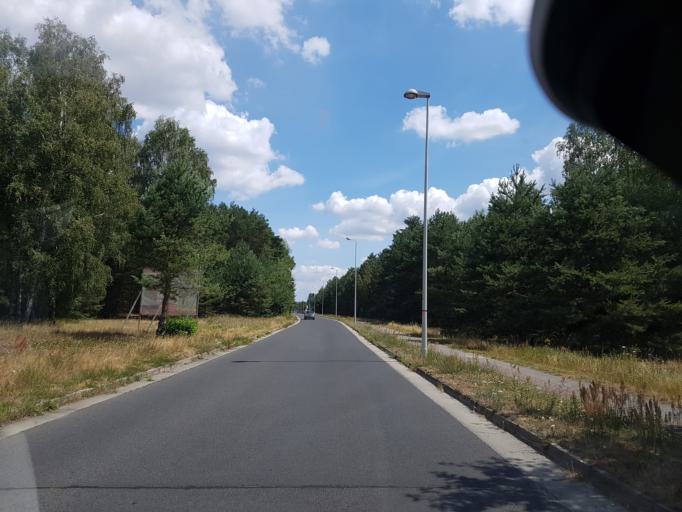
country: DE
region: Brandenburg
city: Cottbus
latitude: 51.7049
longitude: 14.3466
